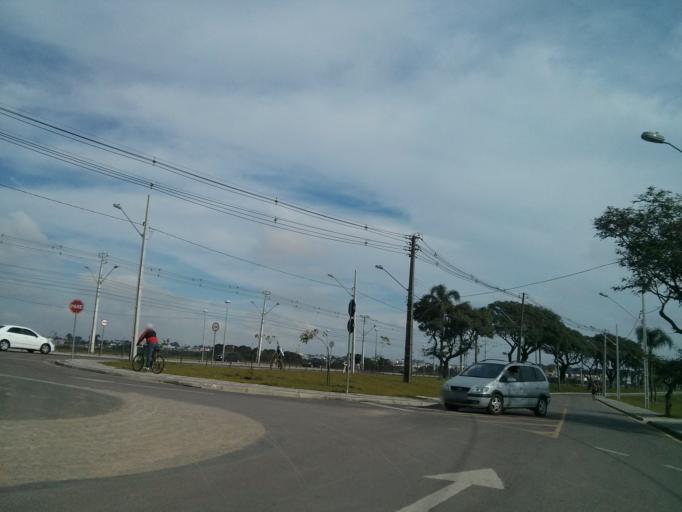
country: BR
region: Parana
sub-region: Sao Jose Dos Pinhais
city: Sao Jose dos Pinhais
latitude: -25.5276
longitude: -49.2200
